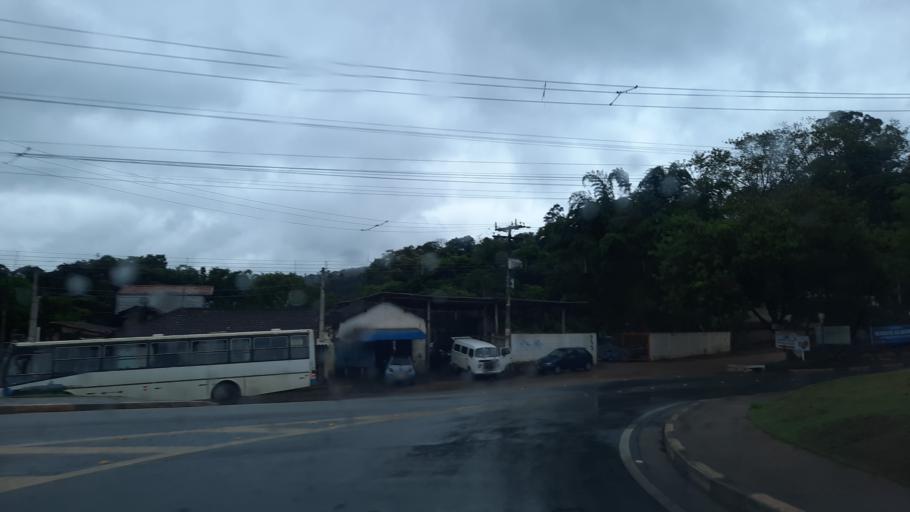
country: BR
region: Sao Paulo
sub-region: Atibaia
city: Atibaia
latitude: -23.0976
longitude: -46.5496
